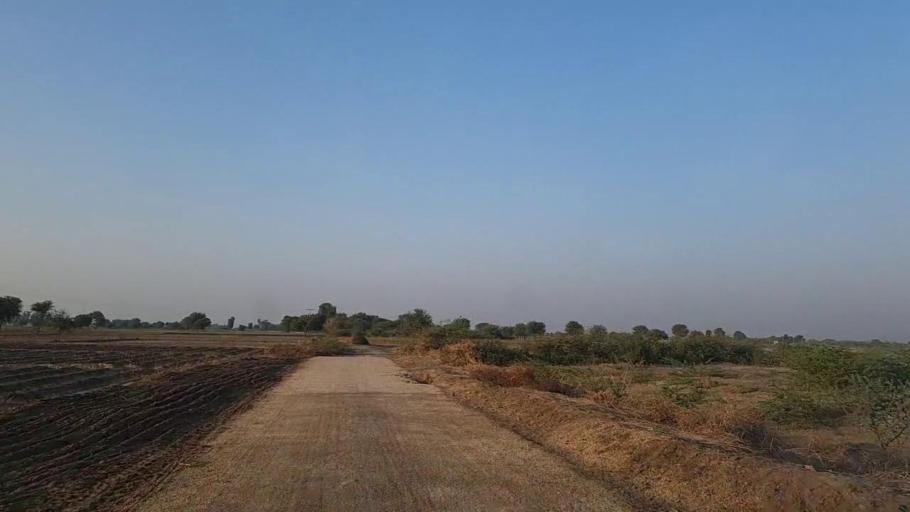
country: PK
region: Sindh
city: Naukot
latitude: 24.9681
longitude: 69.4562
